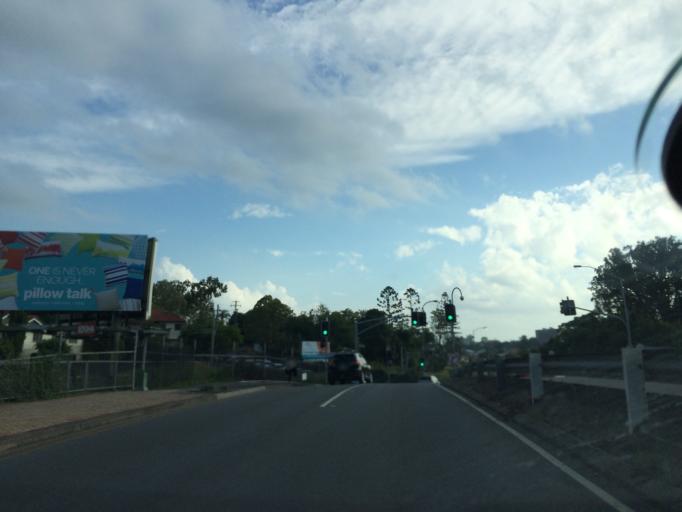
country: AU
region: Queensland
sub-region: Brisbane
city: Toowong
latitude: -27.4879
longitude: 152.9905
